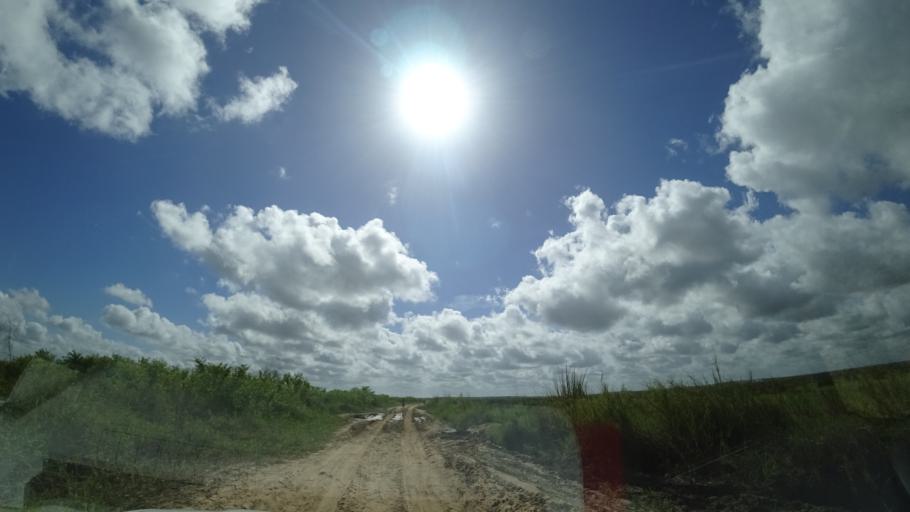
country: MZ
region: Sofala
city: Dondo
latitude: -19.4006
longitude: 34.5682
